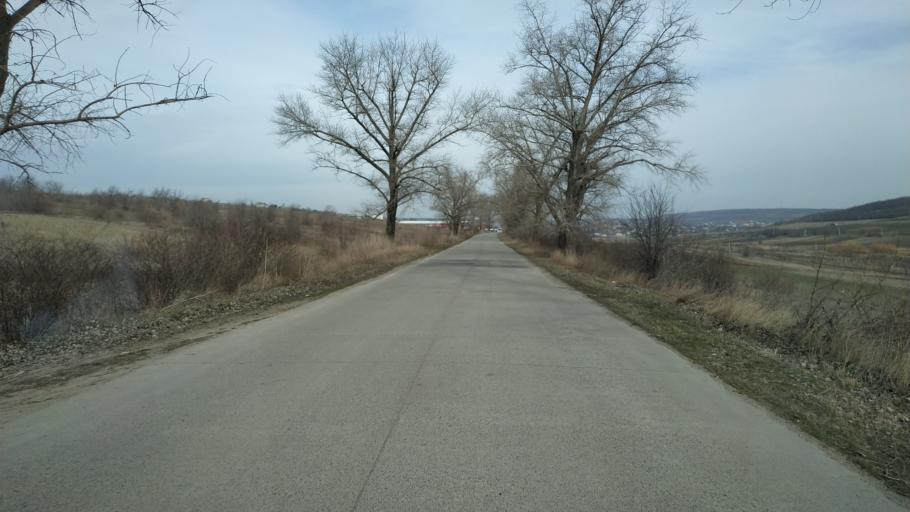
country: MD
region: Chisinau
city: Vatra
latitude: 47.1125
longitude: 28.7237
